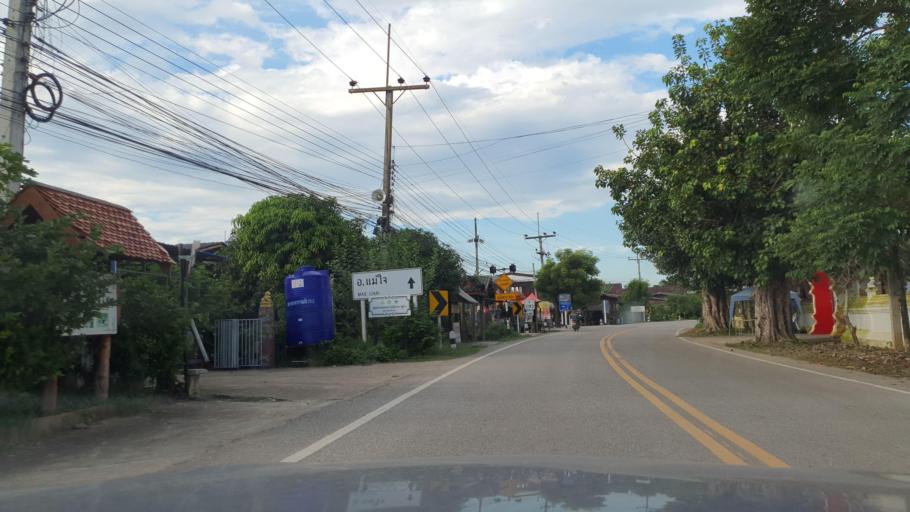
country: TH
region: Phayao
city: Phayao
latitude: 19.1735
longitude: 99.8333
